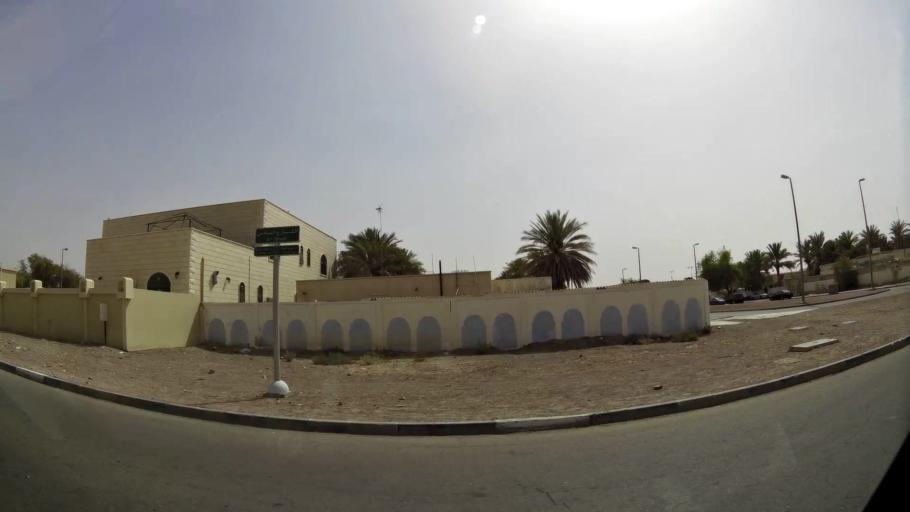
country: AE
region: Abu Dhabi
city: Al Ain
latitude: 24.1863
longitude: 55.6305
